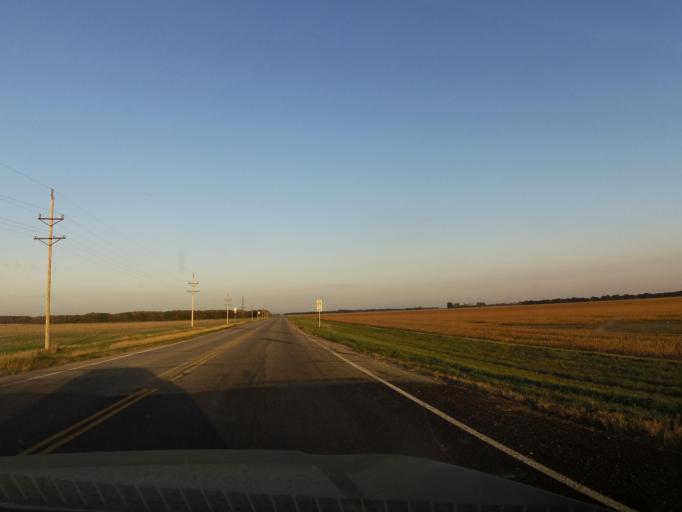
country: CA
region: Manitoba
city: Altona
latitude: 48.9636
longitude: -97.5567
